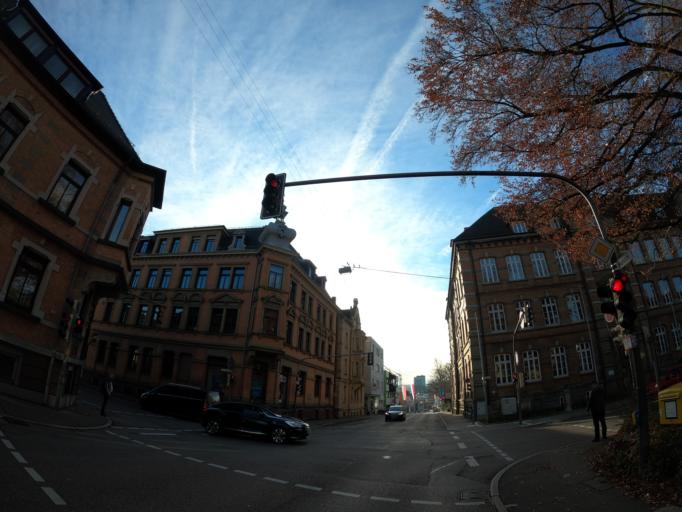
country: DE
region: Baden-Wuerttemberg
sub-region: Regierungsbezirk Stuttgart
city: Goeppingen
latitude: 48.7053
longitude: 9.6555
